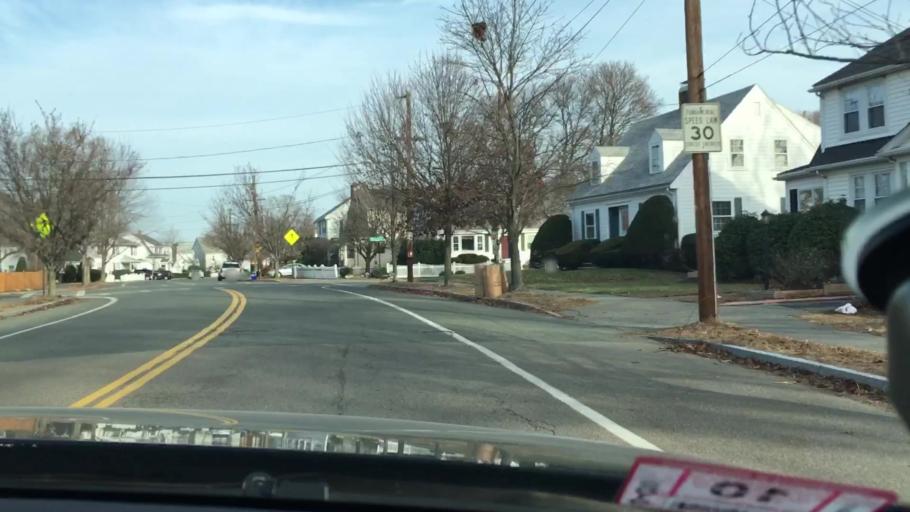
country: US
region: Massachusetts
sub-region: Norfolk County
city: Braintree
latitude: 42.2322
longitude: -71.0021
